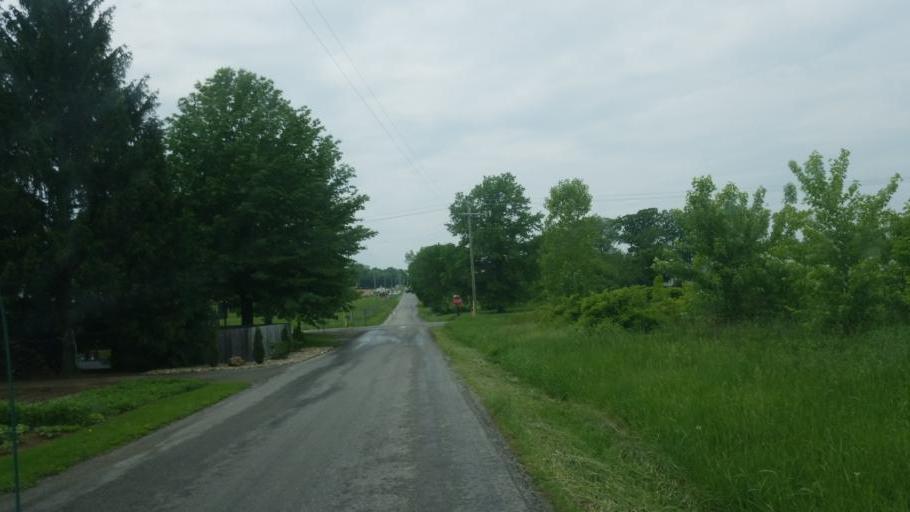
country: US
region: Ohio
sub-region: Wayne County
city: Apple Creek
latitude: 40.7779
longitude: -81.7881
